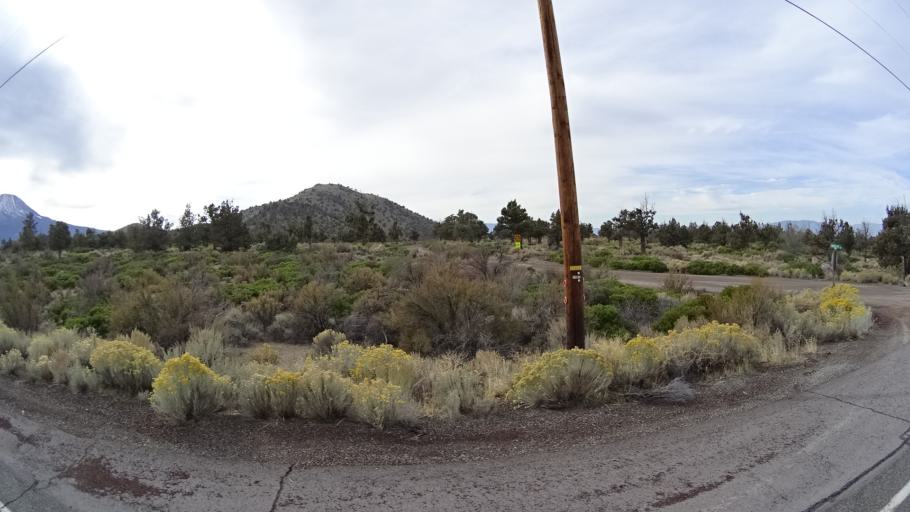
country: US
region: California
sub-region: Siskiyou County
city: Weed
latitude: 41.5557
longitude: -122.2544
